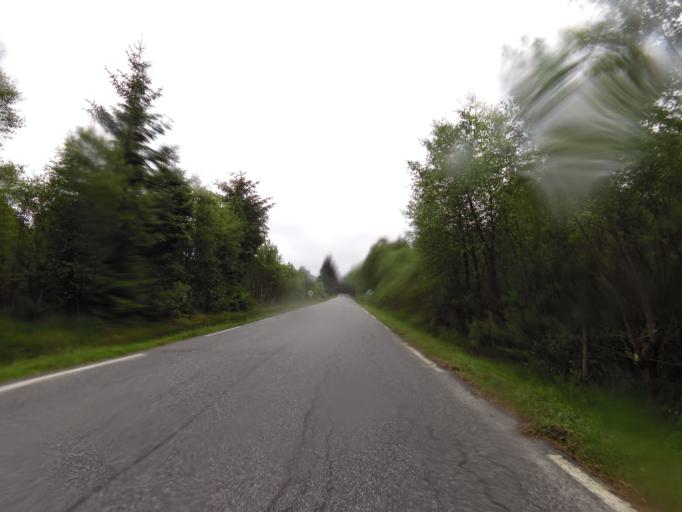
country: NO
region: Hordaland
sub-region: Sveio
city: Sveio
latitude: 59.5217
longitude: 5.2831
